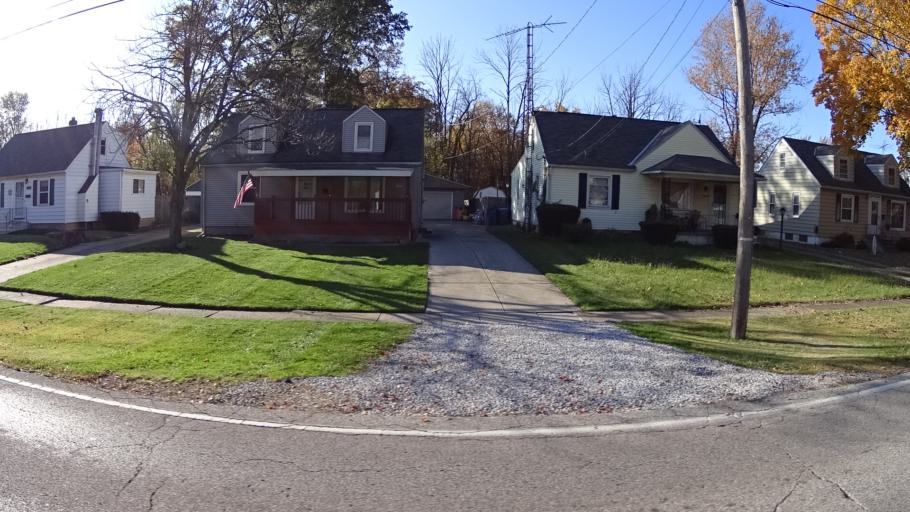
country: US
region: Ohio
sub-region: Lorain County
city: Sheffield Lake
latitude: 41.4712
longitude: -82.1322
